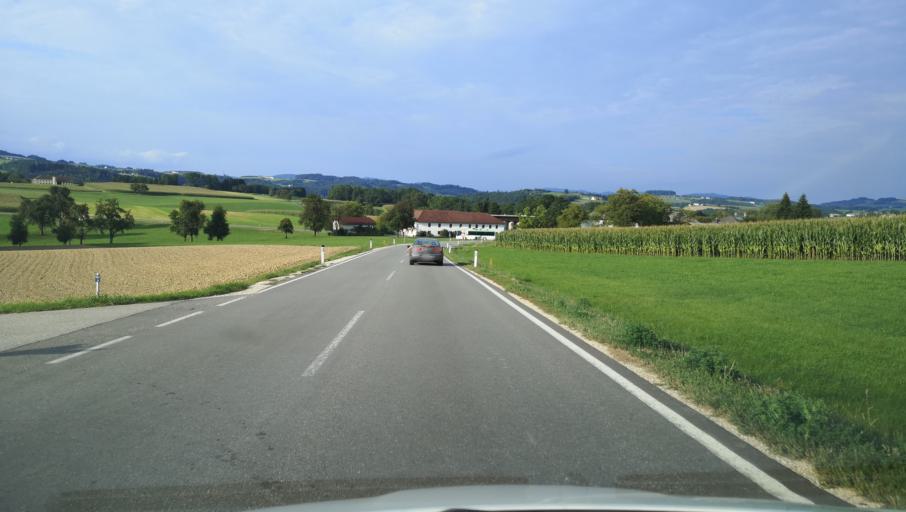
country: AT
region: Lower Austria
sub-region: Politischer Bezirk Amstetten
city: Amstetten
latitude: 48.1582
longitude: 14.9053
